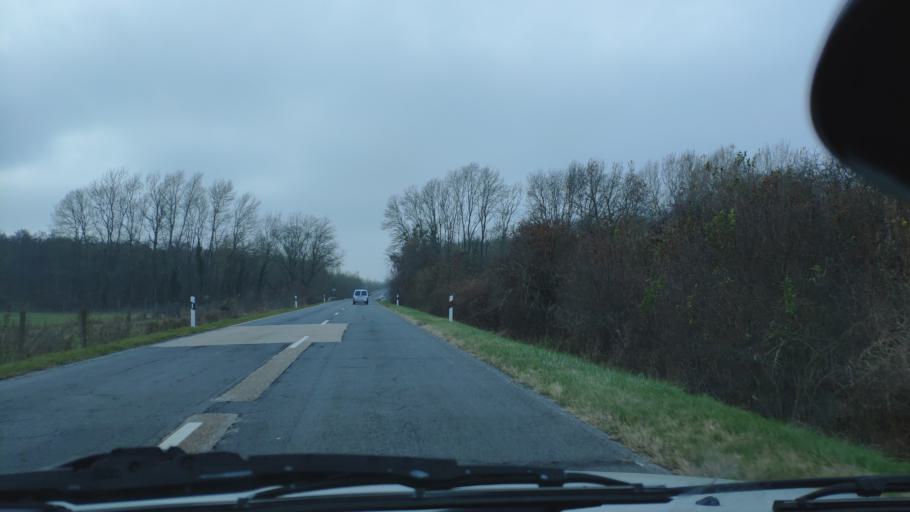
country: HU
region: Zala
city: Zalakomar
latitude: 46.5328
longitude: 17.2153
